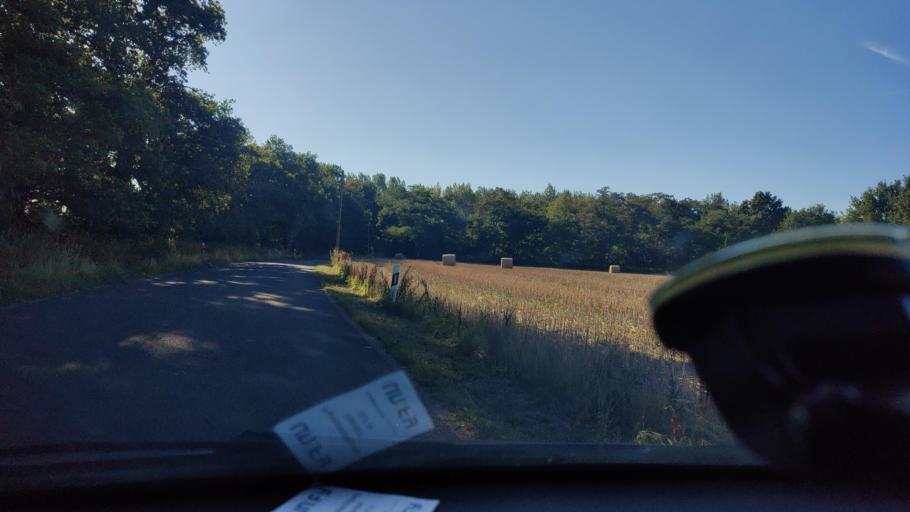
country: DE
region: North Rhine-Westphalia
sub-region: Regierungsbezirk Dusseldorf
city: Goch
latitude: 51.6634
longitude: 6.0871
